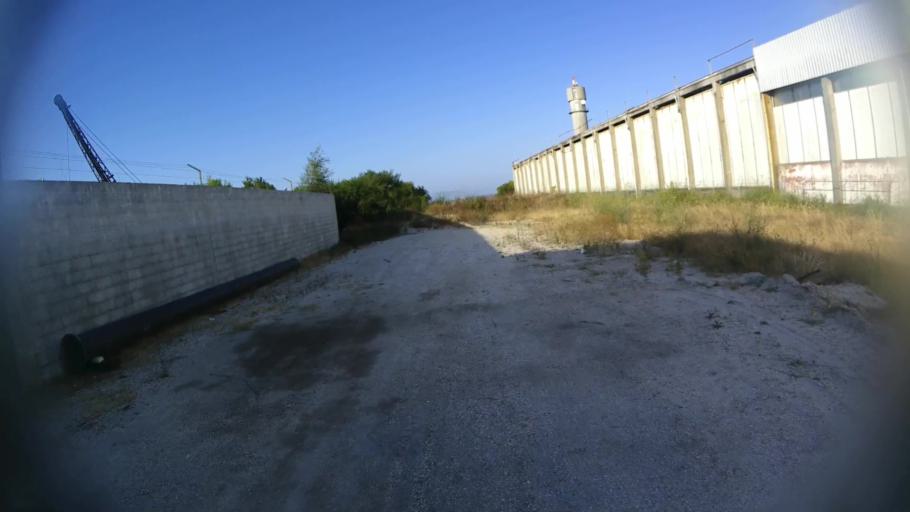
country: PT
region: Aveiro
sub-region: Ilhavo
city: Gafanha da Nazare
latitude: 40.6492
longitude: -8.7019
